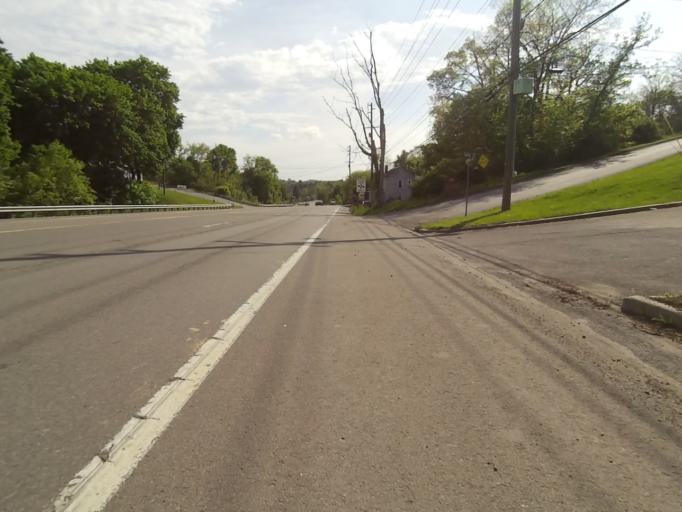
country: US
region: Pennsylvania
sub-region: Centre County
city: Lemont
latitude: 40.8225
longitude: -77.8139
